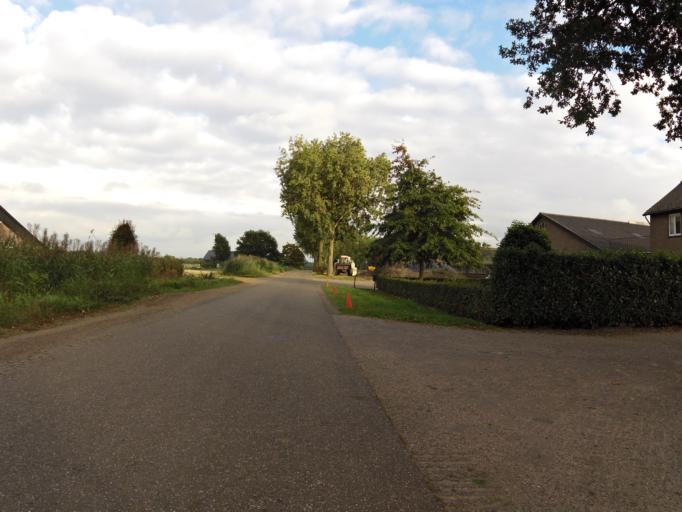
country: NL
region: North Brabant
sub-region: Gemeente Vught
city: Vught
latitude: 51.6839
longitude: 5.2268
